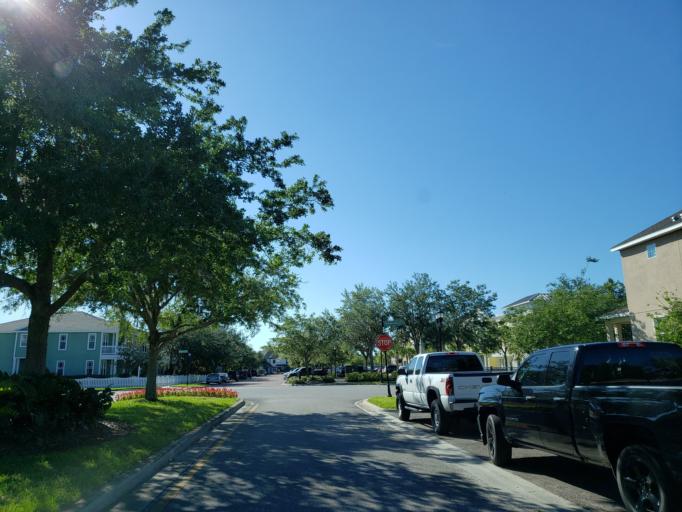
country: US
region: Florida
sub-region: Hillsborough County
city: Fish Hawk
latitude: 27.8412
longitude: -82.2145
